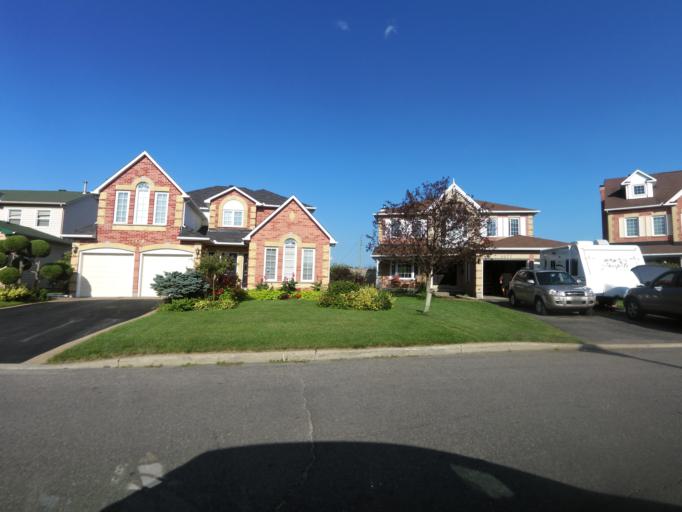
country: CA
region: Ontario
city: Clarence-Rockland
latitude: 45.4849
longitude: -75.4764
